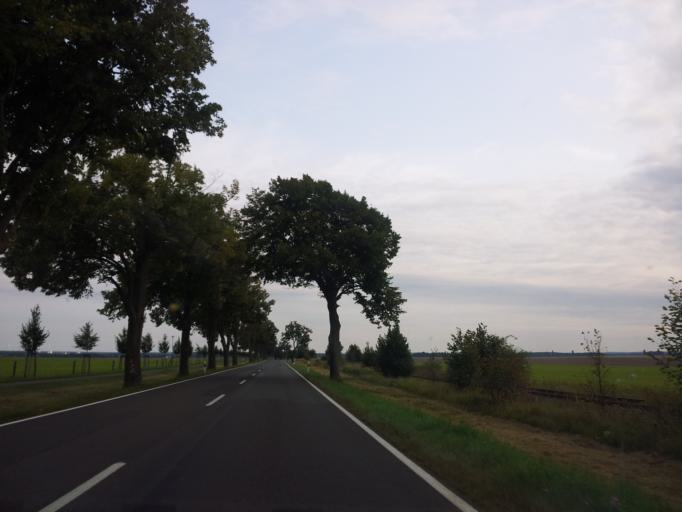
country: DE
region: Brandenburg
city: Belzig
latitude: 52.1191
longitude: 12.6422
